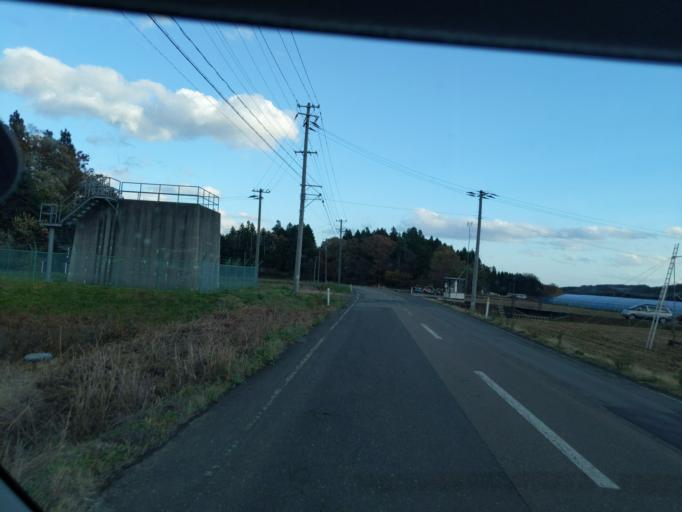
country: JP
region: Iwate
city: Mizusawa
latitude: 39.0806
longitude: 141.0357
